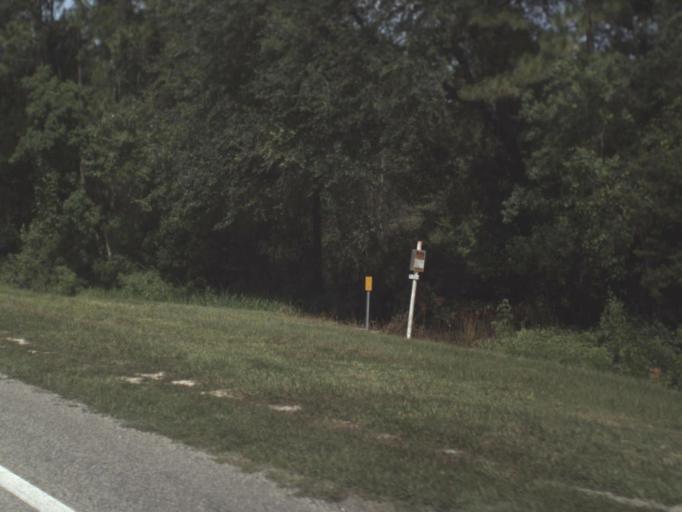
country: US
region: Florida
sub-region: Alachua County
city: Waldo
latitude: 29.7520
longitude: -82.2197
